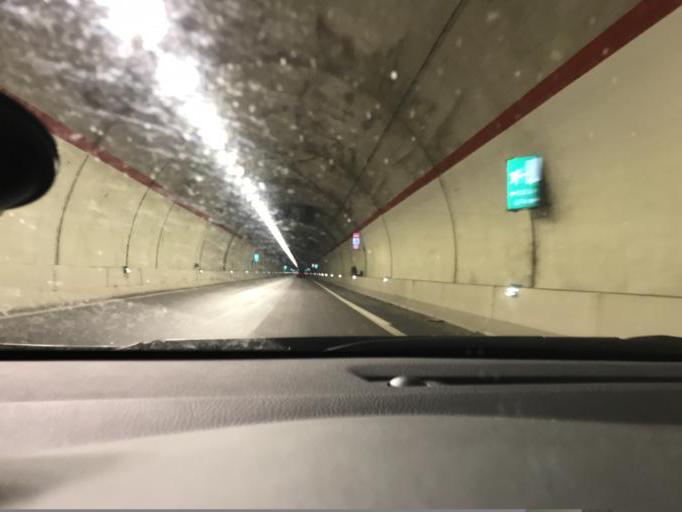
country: IT
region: Umbria
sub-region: Provincia di Perugia
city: Valfabbrica
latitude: 43.1498
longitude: 12.5760
